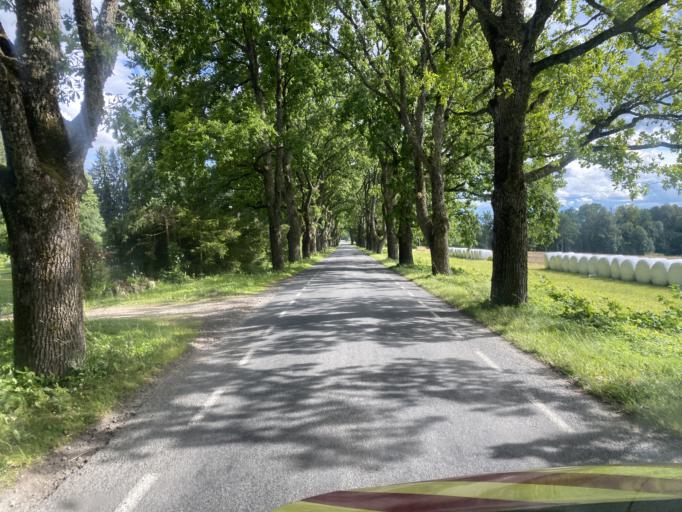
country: EE
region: Viljandimaa
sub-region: Viljandi linn
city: Viljandi
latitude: 58.3978
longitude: 25.6070
